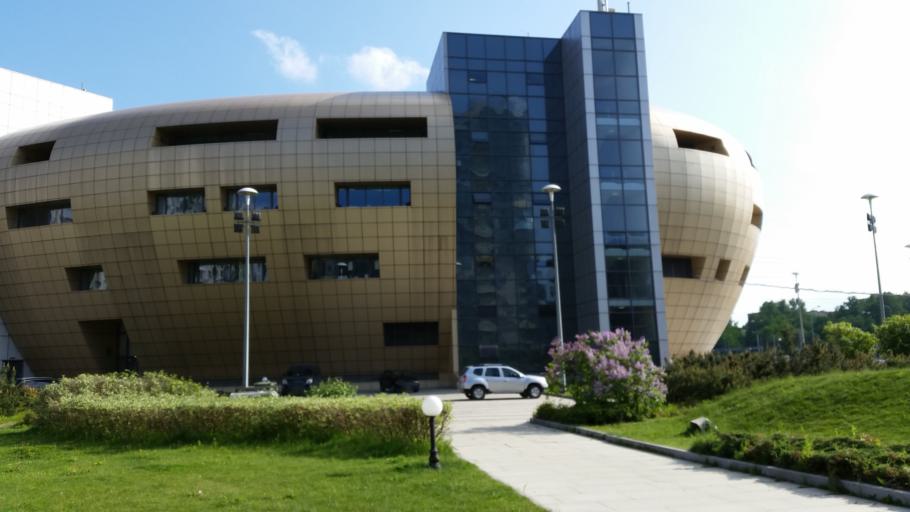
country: RU
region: St.-Petersburg
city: Sosnovaya Polyana
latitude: 59.8492
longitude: 30.1488
